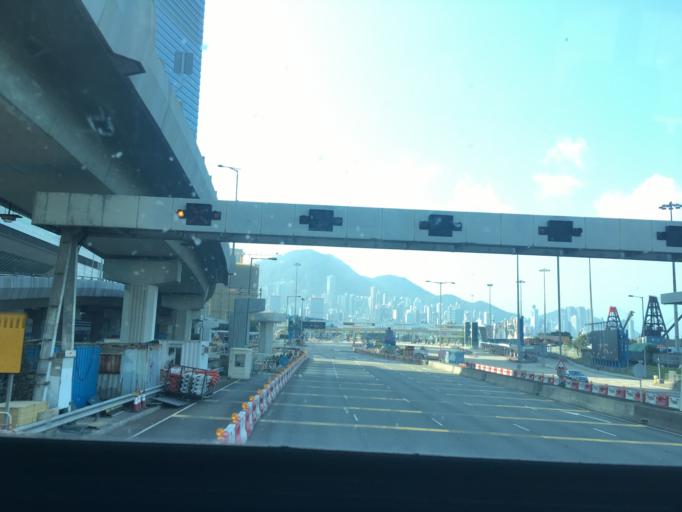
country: HK
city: Hong Kong
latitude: 22.3066
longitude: 114.1607
